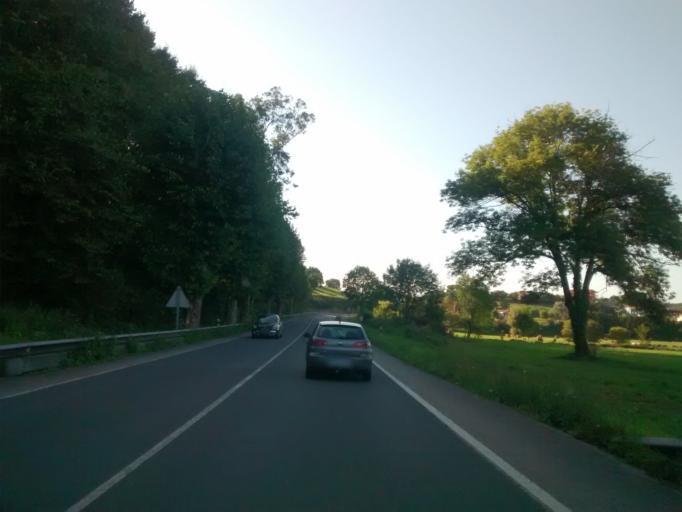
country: ES
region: Cantabria
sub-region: Provincia de Cantabria
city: Puente Viesgo
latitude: 43.3161
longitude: -3.9602
